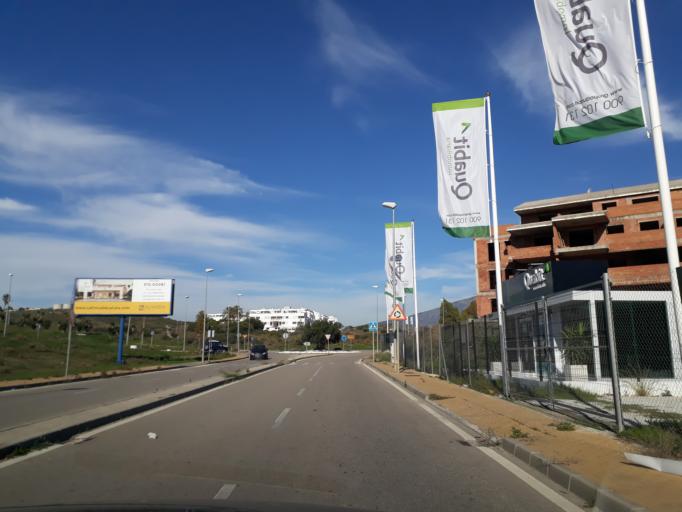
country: ES
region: Andalusia
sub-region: Provincia de Malaga
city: Fuengirola
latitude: 36.5242
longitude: -4.6866
